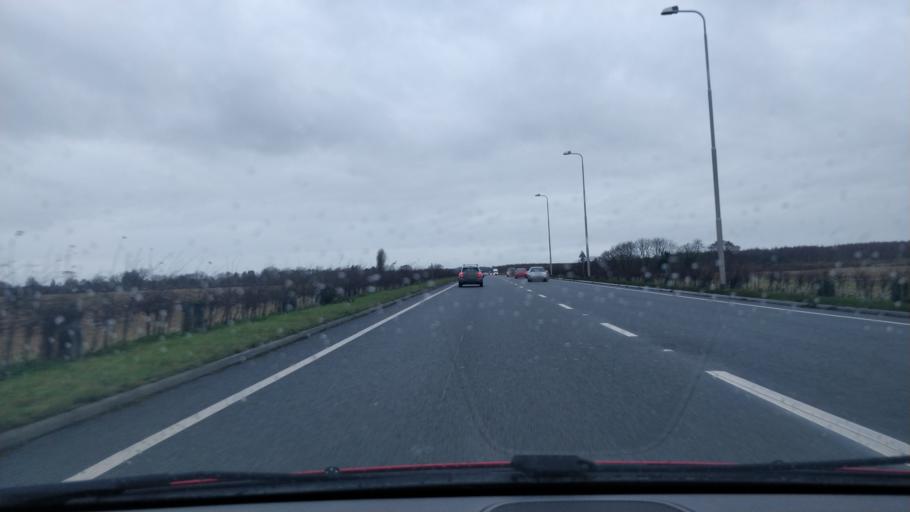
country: GB
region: England
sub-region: Sefton
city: Thornton
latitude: 53.4987
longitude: -2.9831
